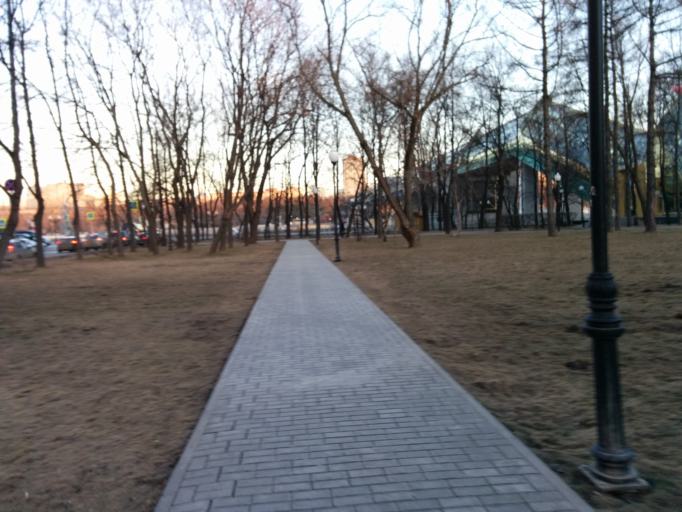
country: RU
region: Moscow
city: Novyye Cheremushki
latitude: 55.7263
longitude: 37.5887
